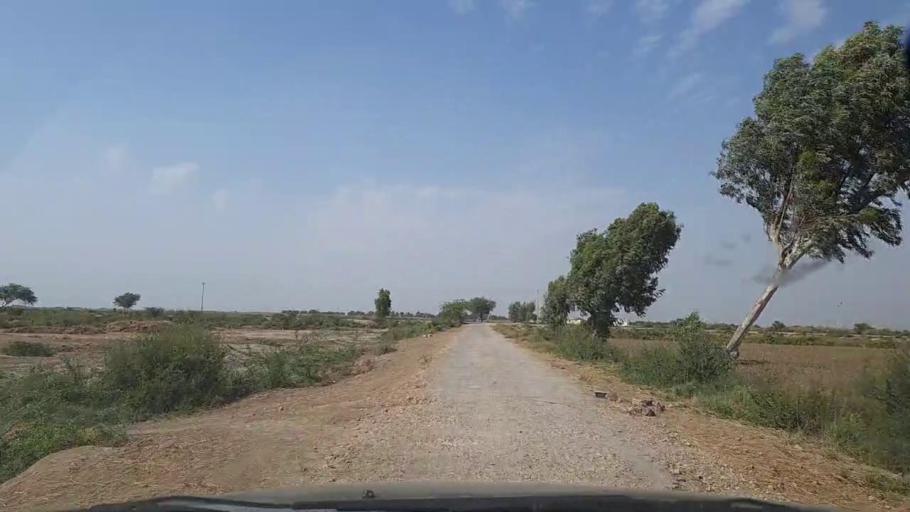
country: PK
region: Sindh
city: Mirpur Batoro
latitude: 24.5943
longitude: 68.2076
